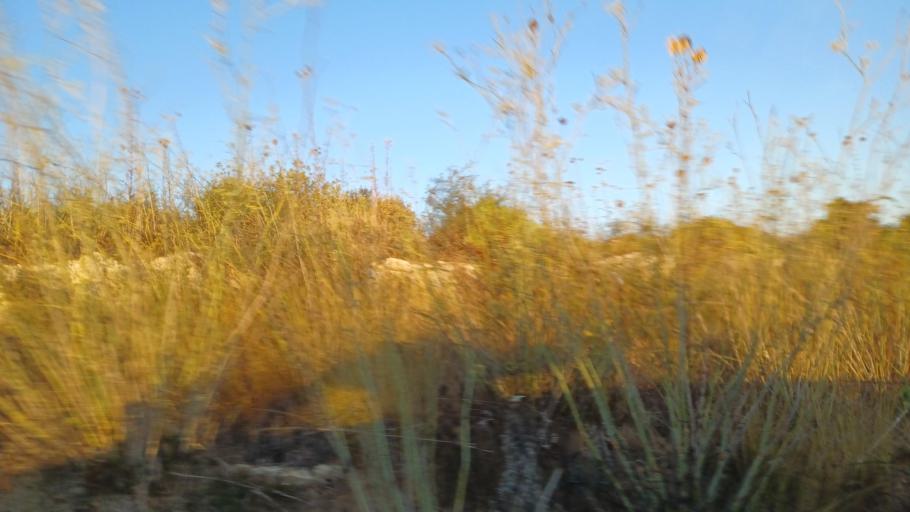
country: CY
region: Pafos
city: Mesogi
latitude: 34.8669
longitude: 32.5183
